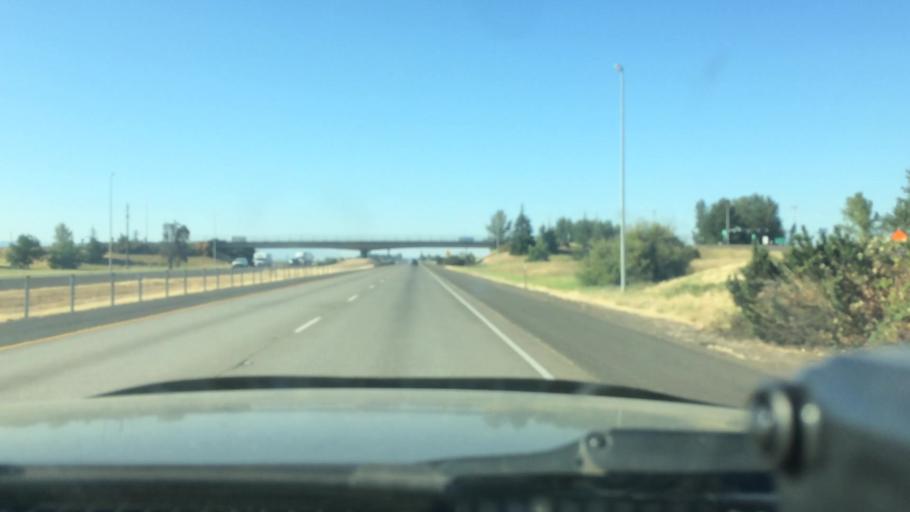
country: US
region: Oregon
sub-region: Linn County
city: Tangent
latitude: 44.5586
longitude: -123.0622
